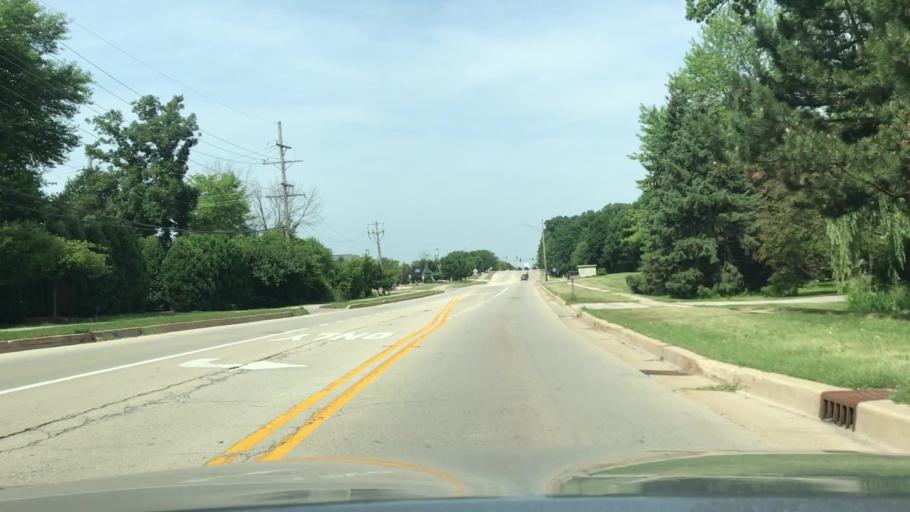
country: US
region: Illinois
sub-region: DuPage County
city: Darien
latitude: 41.7367
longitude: -88.0067
